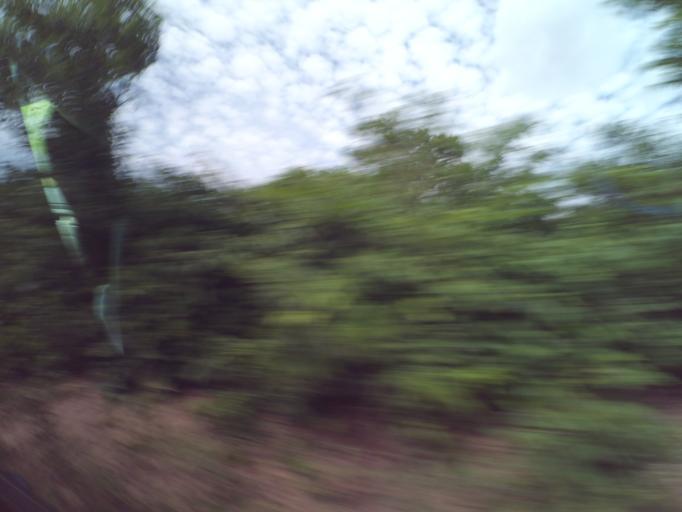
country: BO
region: Santa Cruz
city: Santa Cruz de la Sierra
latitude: -17.9244
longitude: -63.1609
